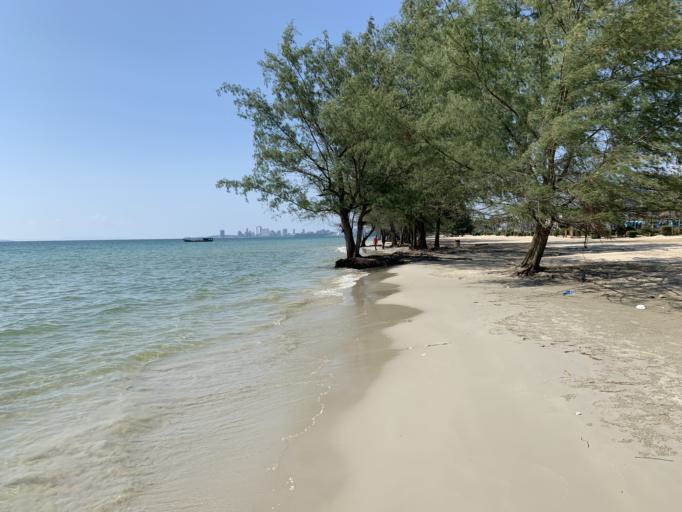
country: KH
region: Preah Sihanouk
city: Sihanoukville
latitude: 10.5635
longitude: 103.5562
